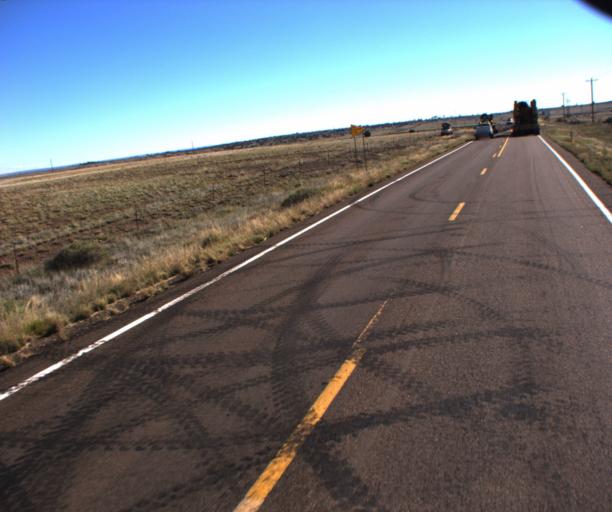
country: US
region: Arizona
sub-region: Apache County
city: Saint Johns
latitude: 34.5104
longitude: -109.4520
